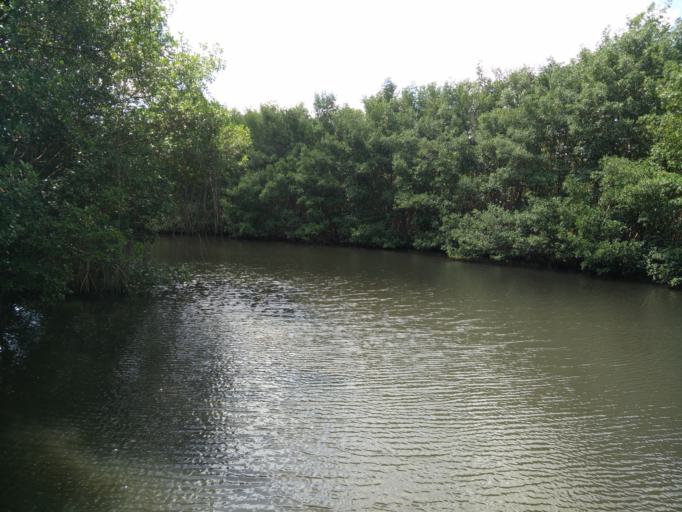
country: GP
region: Guadeloupe
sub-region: Guadeloupe
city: Petit-Canal
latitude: 16.3523
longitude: -61.4899
